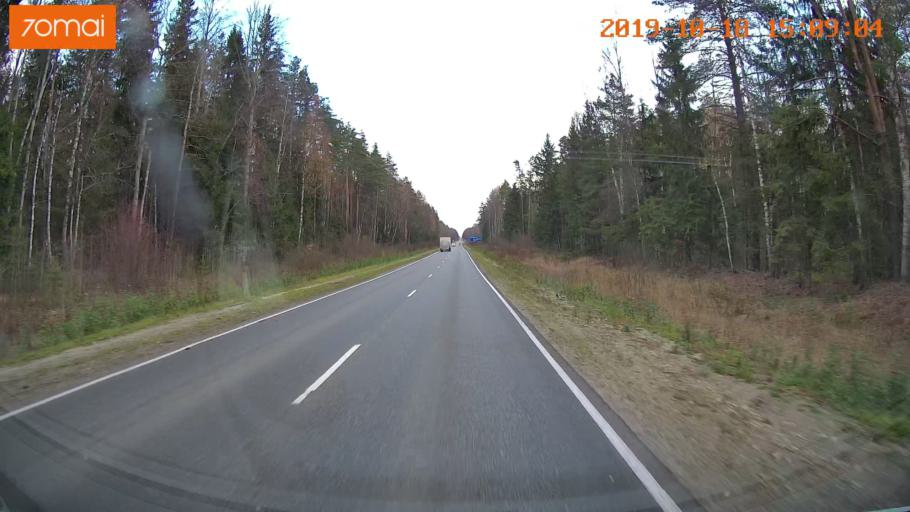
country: RU
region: Vladimir
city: Gus'-Khrustal'nyy
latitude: 55.5611
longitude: 40.6172
